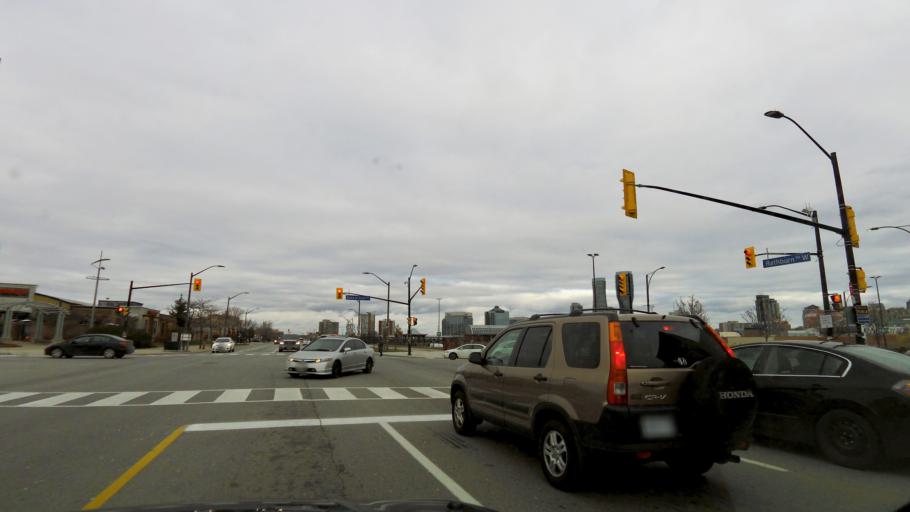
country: CA
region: Ontario
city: Mississauga
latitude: 43.5925
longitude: -79.6491
